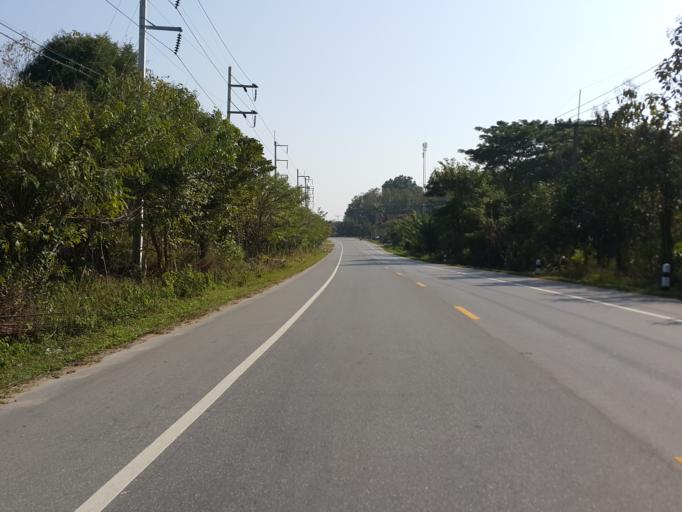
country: TH
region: Lampang
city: Chae Hom
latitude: 18.6495
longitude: 99.5373
